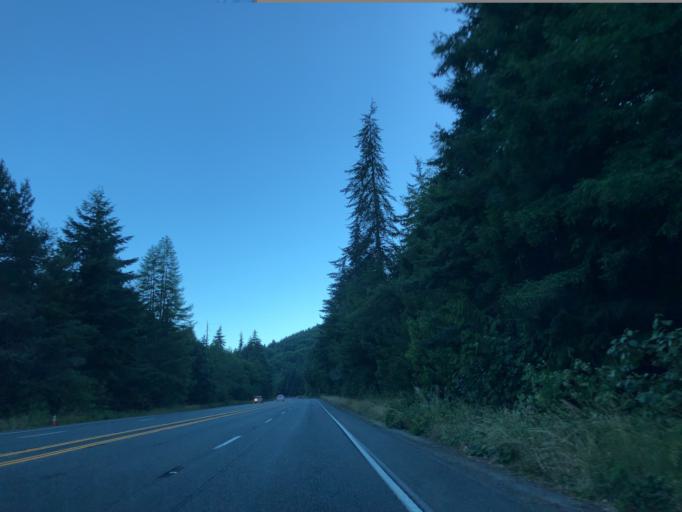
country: US
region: California
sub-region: Del Norte County
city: Bertsch-Oceanview
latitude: 41.5000
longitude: -124.0370
